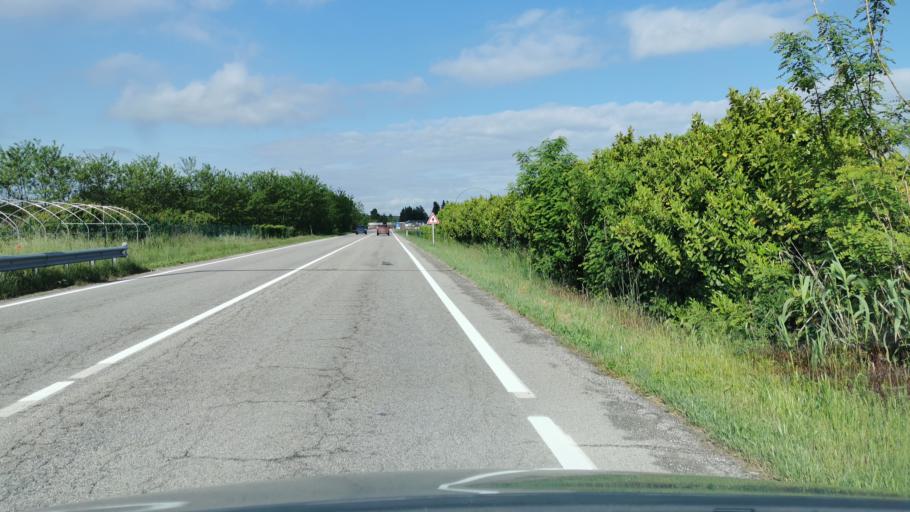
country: IT
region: Piedmont
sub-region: Provincia di Torino
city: Santena
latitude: 44.9381
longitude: 7.7682
